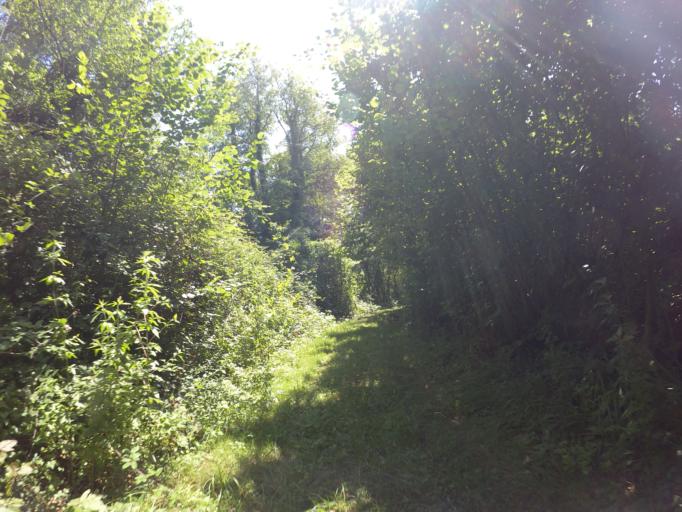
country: IT
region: Friuli Venezia Giulia
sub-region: Provincia di Udine
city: Bertiolo
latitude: 45.9279
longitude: 13.0834
